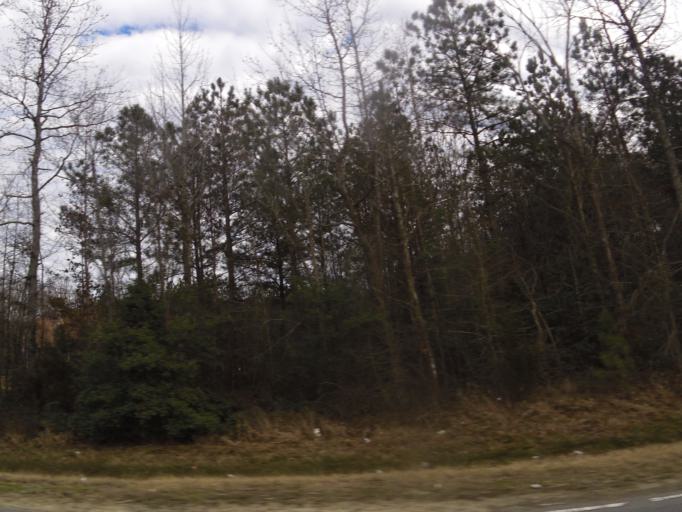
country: US
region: North Carolina
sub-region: Hertford County
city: Winton
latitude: 36.5282
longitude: -76.9800
